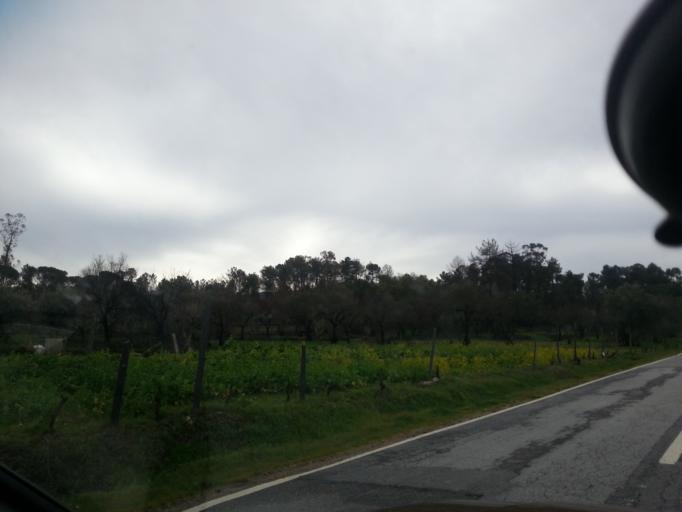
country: PT
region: Guarda
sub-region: Seia
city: Seia
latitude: 40.4826
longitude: -7.6642
